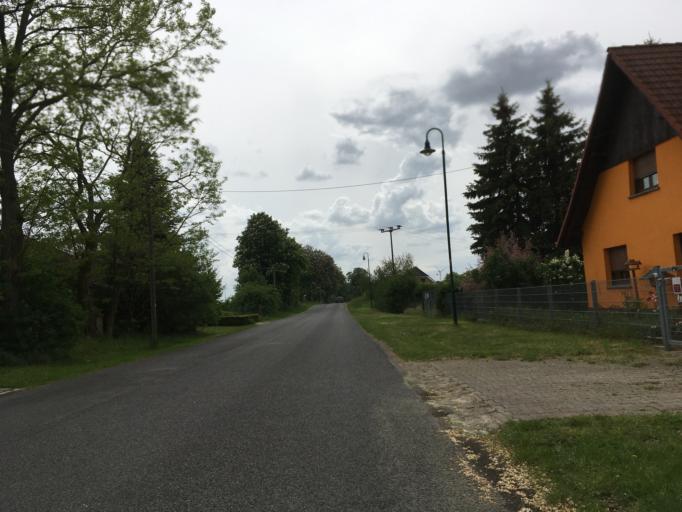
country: DE
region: Brandenburg
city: Melchow
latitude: 52.7176
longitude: 13.7342
